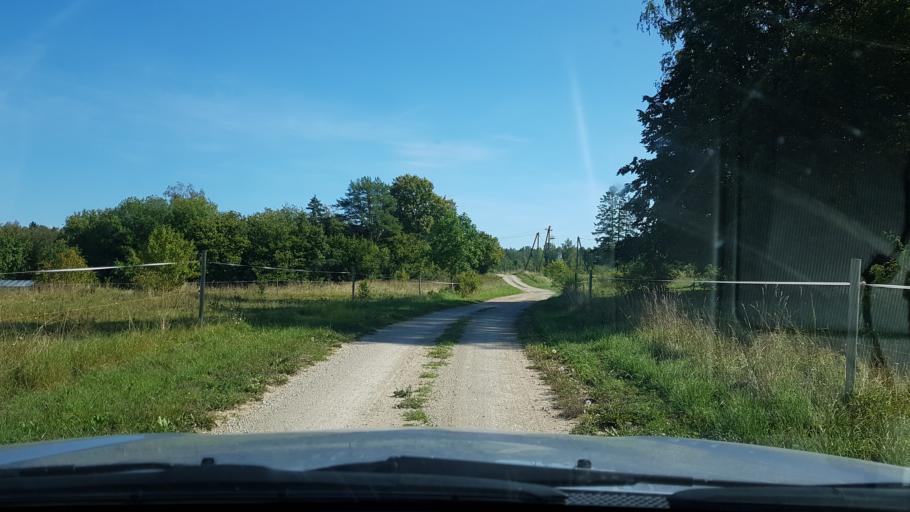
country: EE
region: Ida-Virumaa
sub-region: Sillamaee linn
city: Sillamae
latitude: 59.3931
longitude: 27.8586
